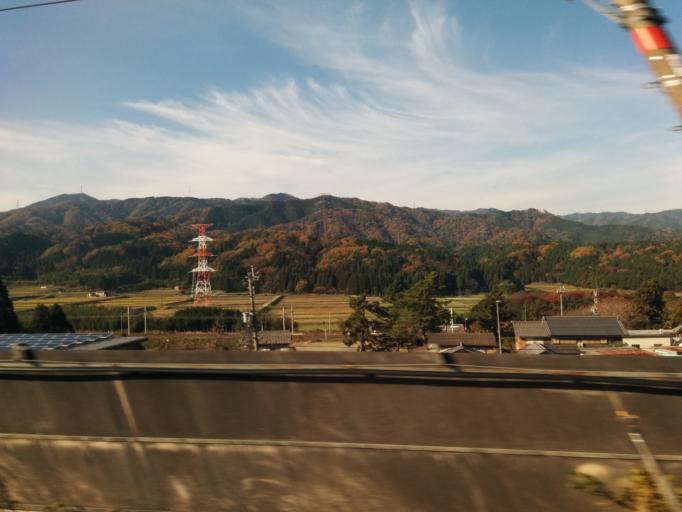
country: JP
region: Gifu
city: Tarui
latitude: 35.3665
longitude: 136.4932
